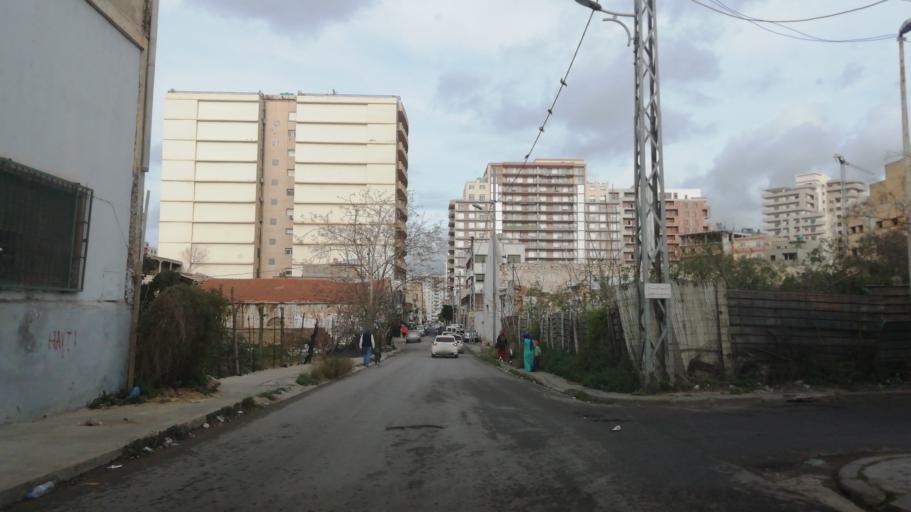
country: DZ
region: Oran
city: Oran
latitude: 35.7003
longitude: -0.6253
